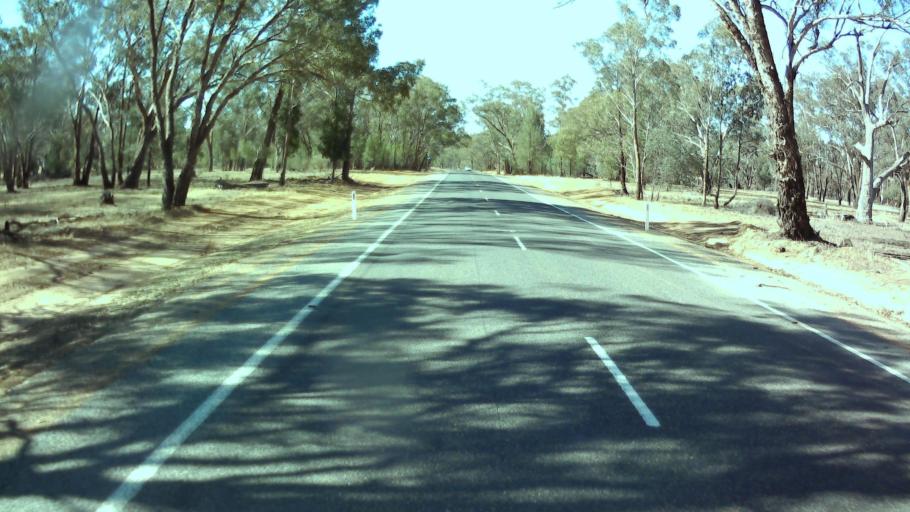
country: AU
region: New South Wales
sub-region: Weddin
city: Grenfell
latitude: -33.7613
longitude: 148.0821
